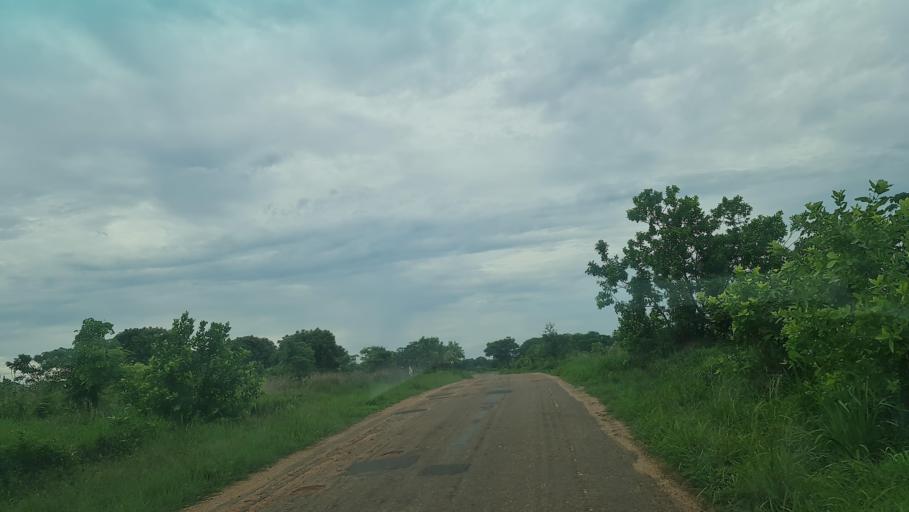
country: MW
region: Southern Region
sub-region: Nsanje District
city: Nsanje
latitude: -17.6894
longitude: 35.7323
